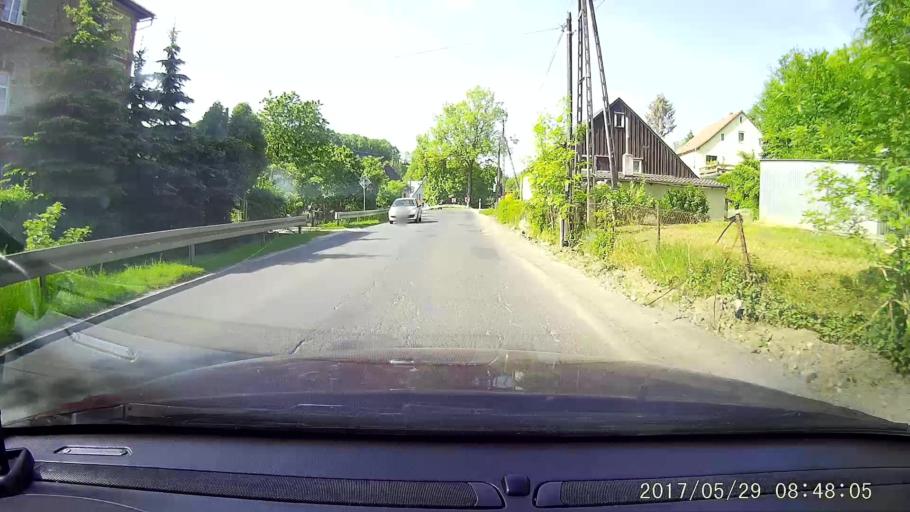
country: PL
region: Lower Silesian Voivodeship
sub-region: Powiat jeleniogorski
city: Jezow Sudecki
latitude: 50.9445
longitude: 15.8007
